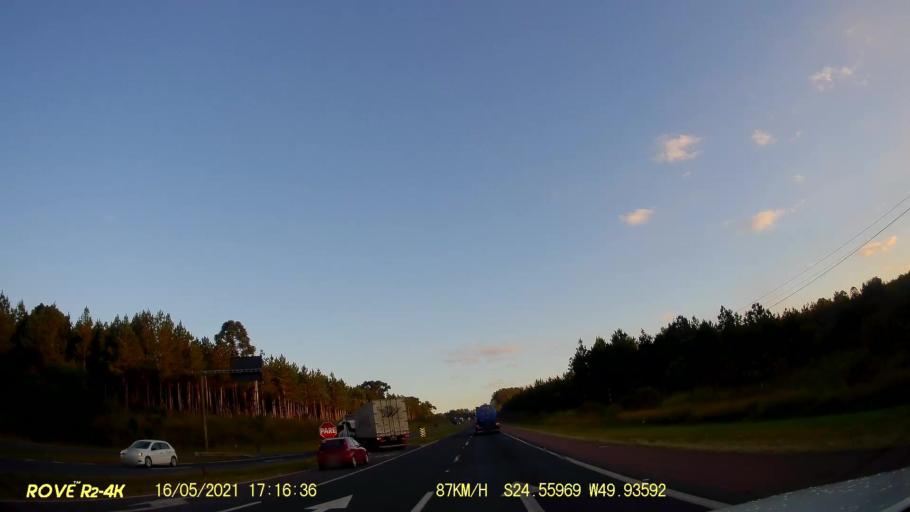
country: BR
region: Parana
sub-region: Pirai Do Sul
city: Pirai do Sul
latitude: -24.5600
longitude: -49.9360
